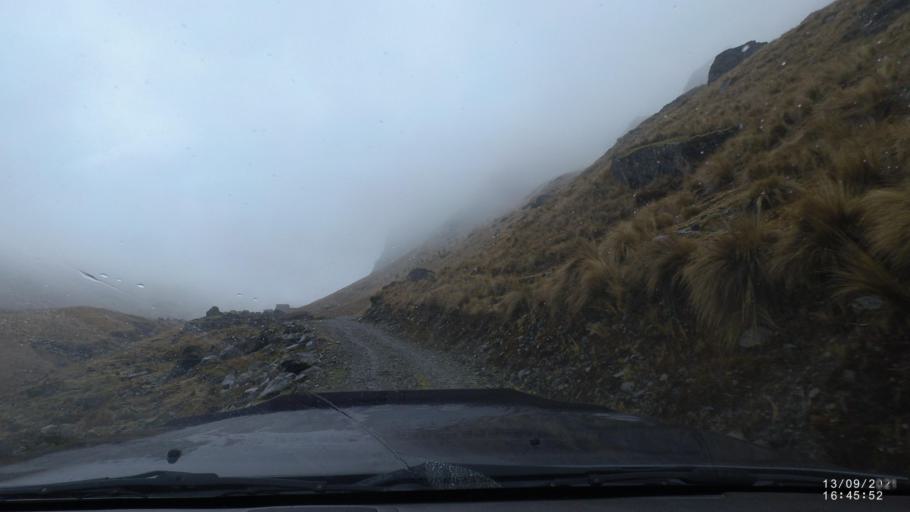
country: BO
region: Cochabamba
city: Colomi
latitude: -17.2947
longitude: -65.7109
